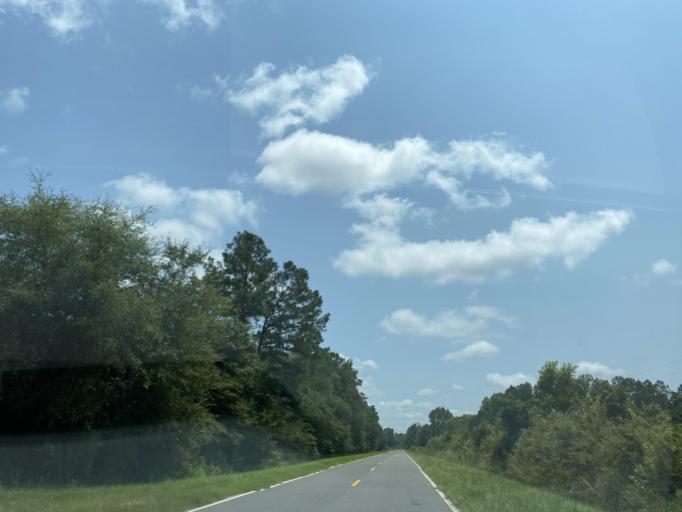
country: US
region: Georgia
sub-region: Telfair County
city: Lumber City
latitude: 31.9536
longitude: -82.6954
